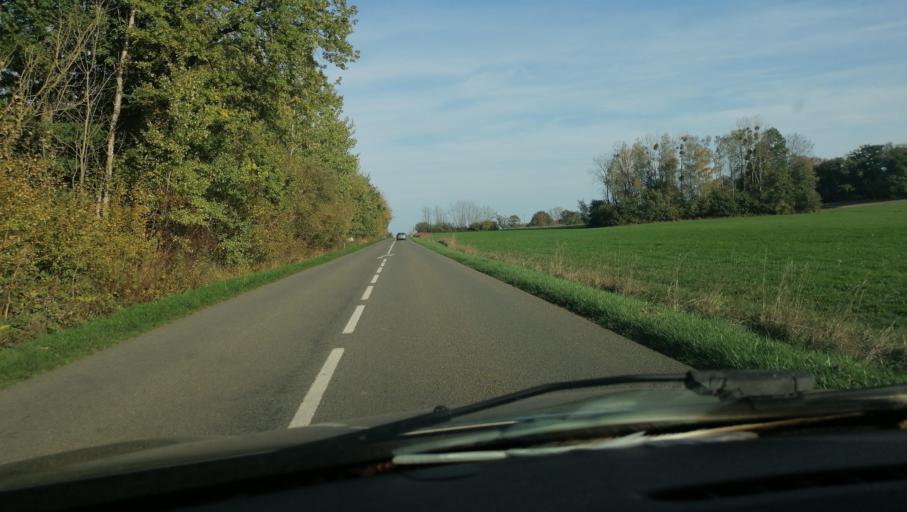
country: FR
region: Champagne-Ardenne
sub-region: Departement des Ardennes
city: La Francheville
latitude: 49.6955
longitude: 4.7236
